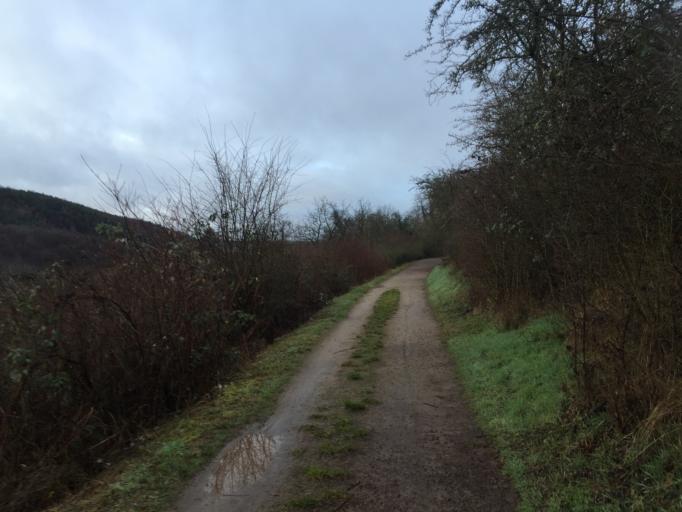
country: DE
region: Rheinland-Pfalz
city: Neuleiningen
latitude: 49.5388
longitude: 8.1253
